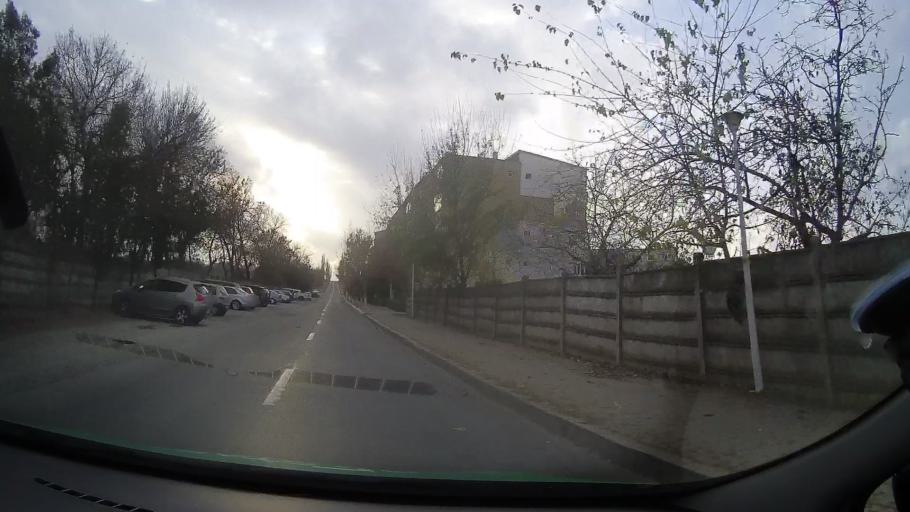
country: RO
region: Constanta
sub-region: Municipiul Medgidia
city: Medgidia
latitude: 44.2422
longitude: 28.2564
